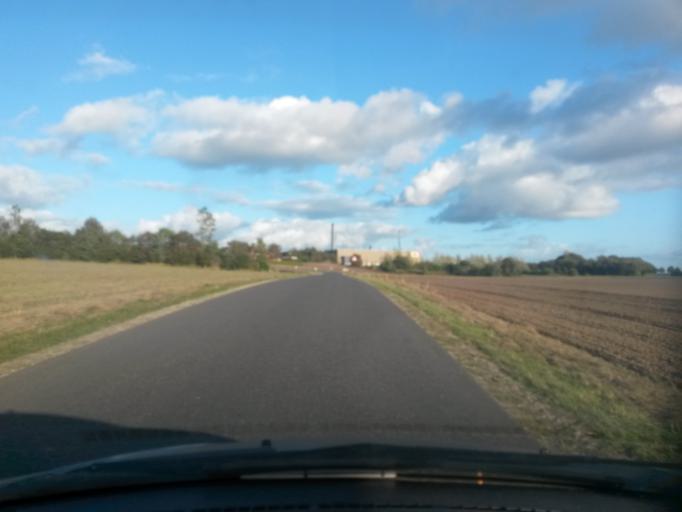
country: DK
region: Central Jutland
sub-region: Viborg Kommune
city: Viborg
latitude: 56.3741
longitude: 9.3861
